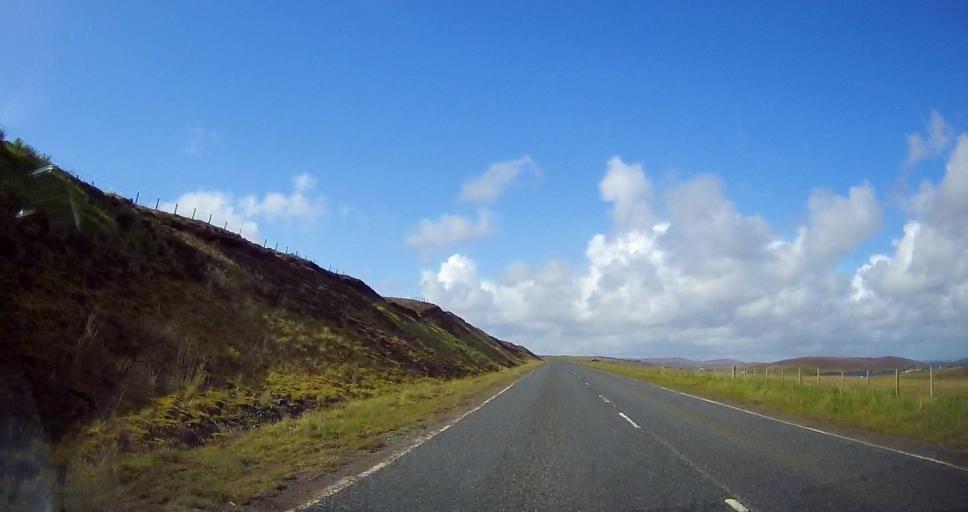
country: GB
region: Scotland
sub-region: Shetland Islands
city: Lerwick
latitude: 60.2170
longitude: -1.2340
